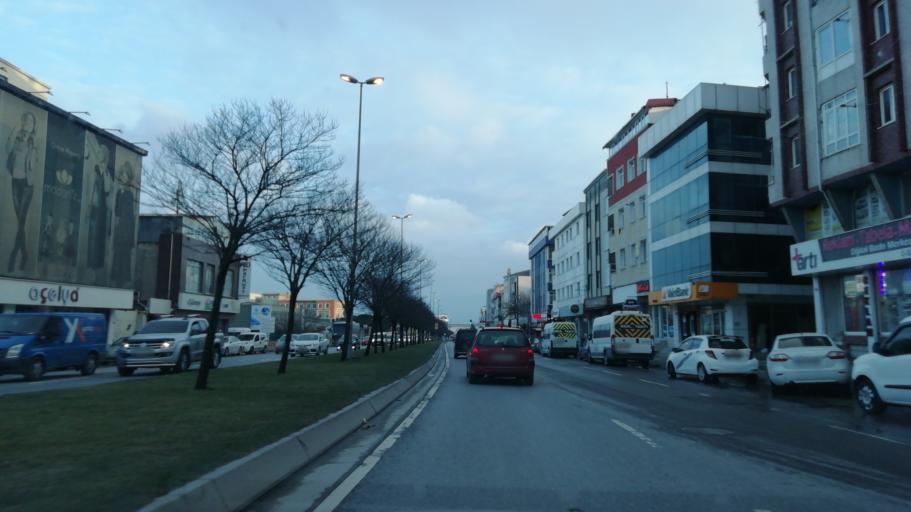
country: TR
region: Istanbul
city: Yakuplu
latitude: 41.0040
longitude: 28.7084
